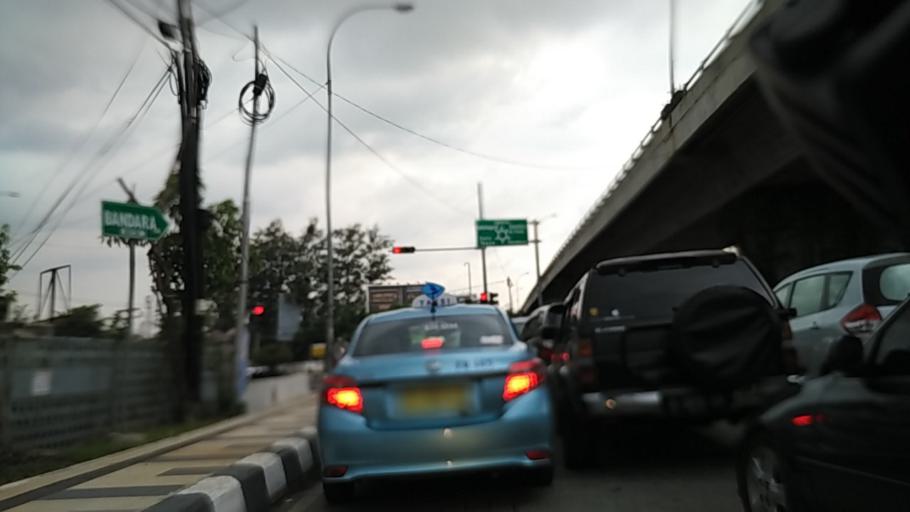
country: ID
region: Central Java
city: Semarang
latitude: -6.9846
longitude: 110.3847
